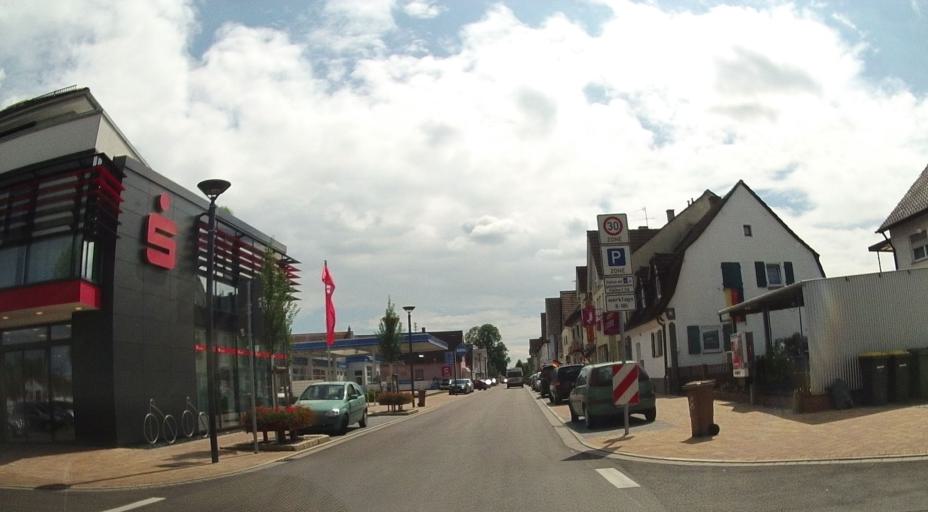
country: DE
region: Baden-Wuerttemberg
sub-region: Karlsruhe Region
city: Durmersheim
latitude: 48.9370
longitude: 8.2723
